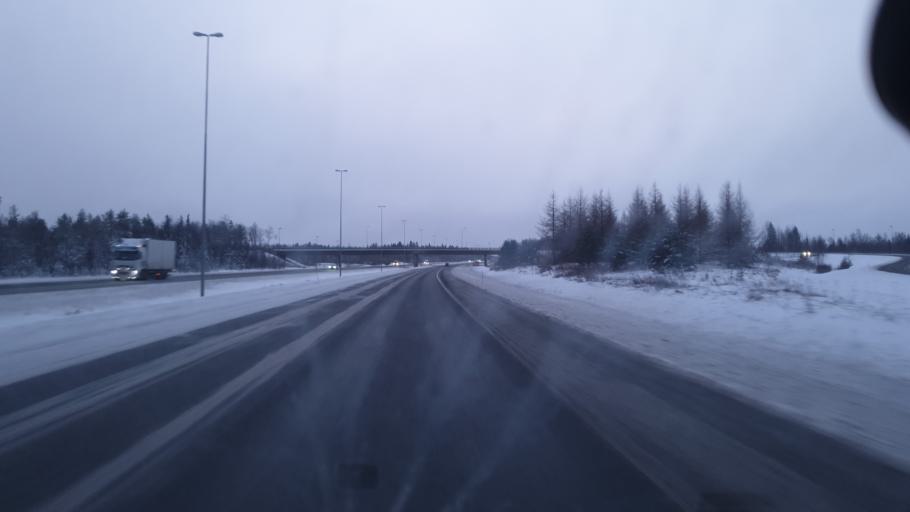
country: FI
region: Lapland
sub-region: Kemi-Tornio
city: Keminmaa
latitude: 65.8193
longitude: 24.4861
